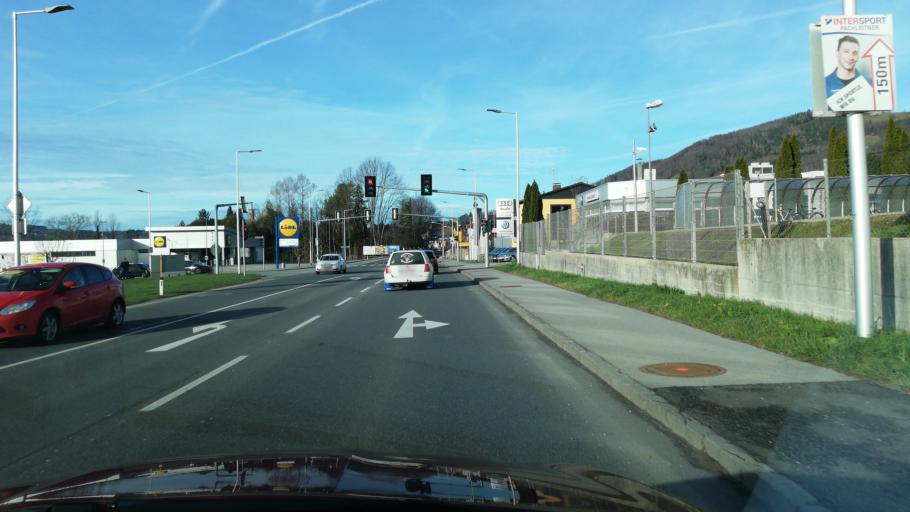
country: AT
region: Upper Austria
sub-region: Politischer Bezirk Kirchdorf an der Krems
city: Micheldorf in Oberoesterreich
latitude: 47.8968
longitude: 14.1276
